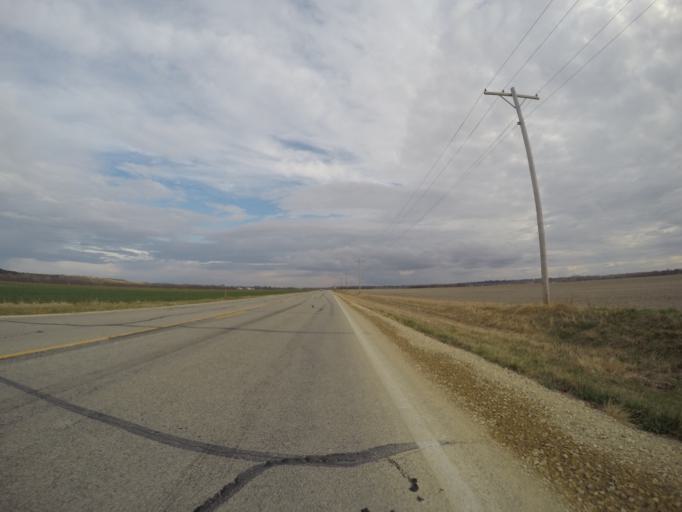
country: US
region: Kansas
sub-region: Riley County
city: Manhattan
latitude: 39.2347
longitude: -96.5683
